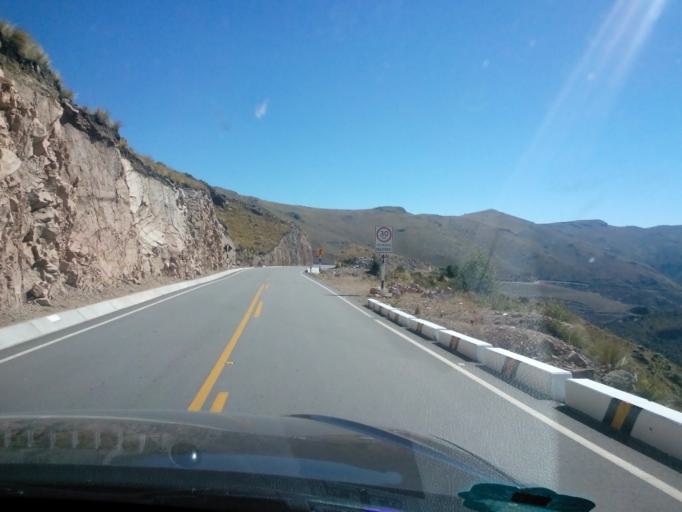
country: PE
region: Ayacucho
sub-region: Provincia de Huamanga
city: Ocros
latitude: -13.3915
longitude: -73.9521
